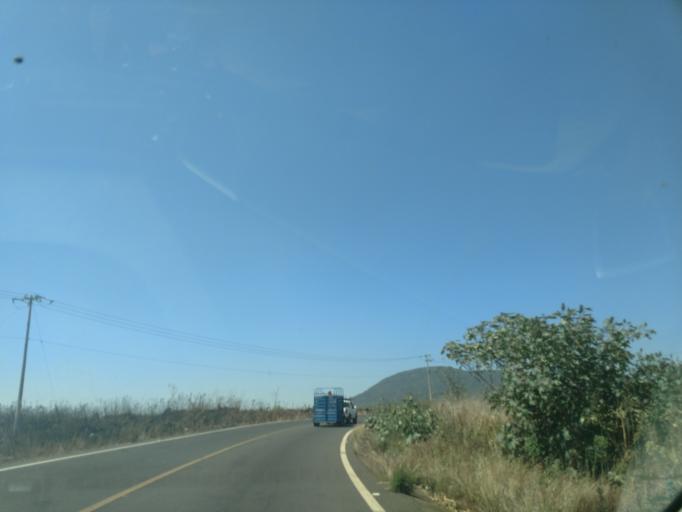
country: MX
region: Nayarit
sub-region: Tepic
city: La Corregidora
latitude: 21.5017
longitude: -104.7565
